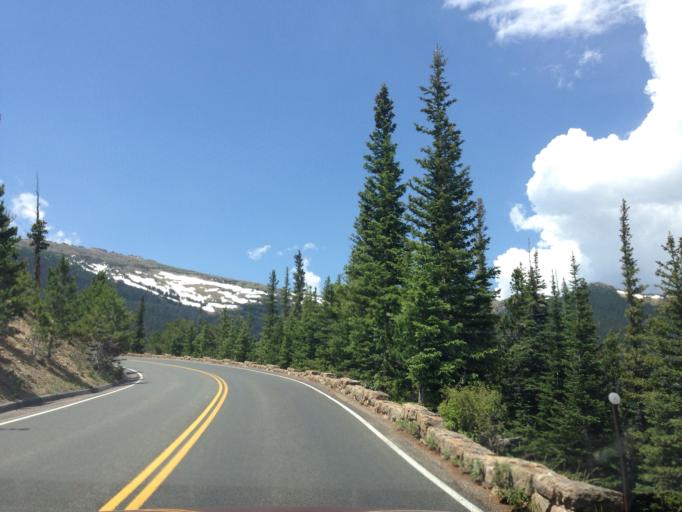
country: US
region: Colorado
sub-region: Larimer County
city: Estes Park
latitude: 40.3932
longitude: -105.6474
